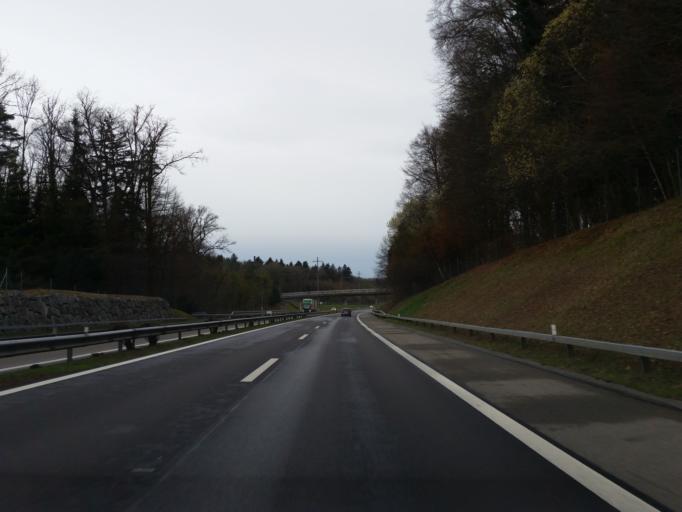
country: CH
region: Thurgau
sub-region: Kreuzlingen District
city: Tagerwilen
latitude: 47.6177
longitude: 9.1097
